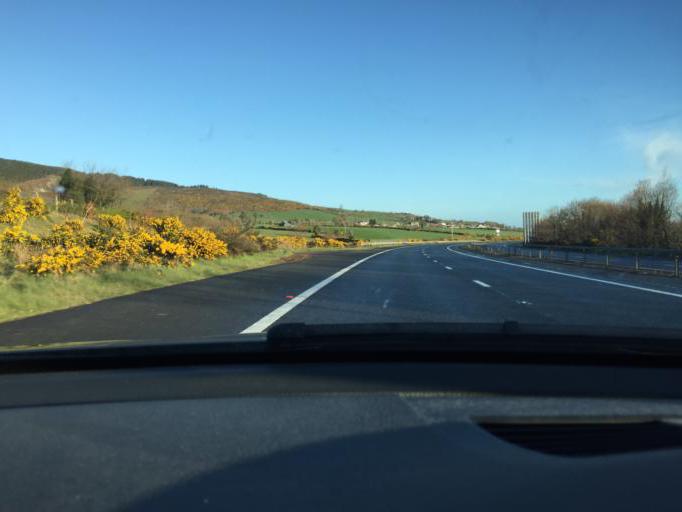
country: GB
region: Northern Ireland
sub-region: Newry and Mourne District
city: Newry
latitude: 54.1594
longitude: -6.3568
